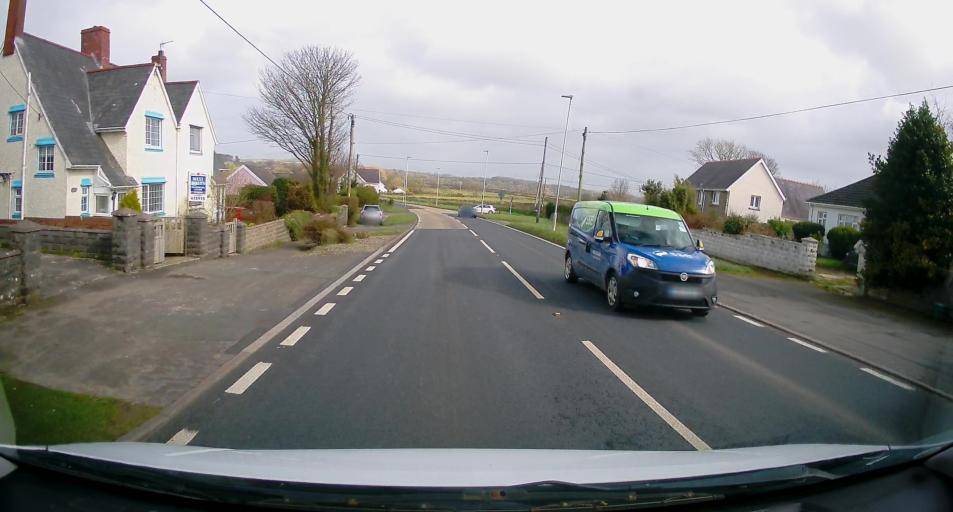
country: GB
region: Wales
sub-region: County of Ceredigion
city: Aberporth
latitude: 52.1094
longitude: -4.5381
